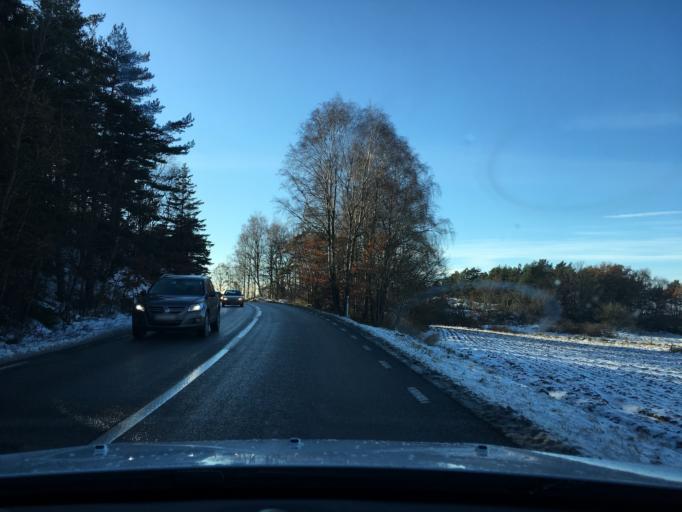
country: SE
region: Vaestra Goetaland
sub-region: Tjorns Kommun
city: Myggenas
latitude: 58.1122
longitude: 11.7003
